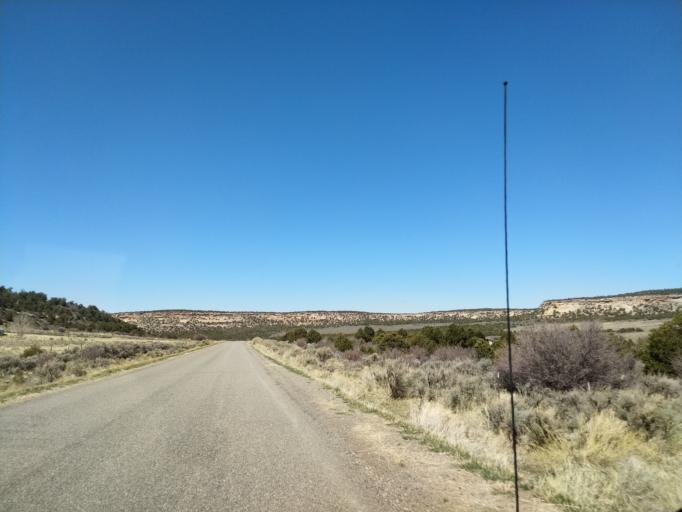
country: US
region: Colorado
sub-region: Mesa County
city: Loma
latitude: 38.9580
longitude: -109.0031
